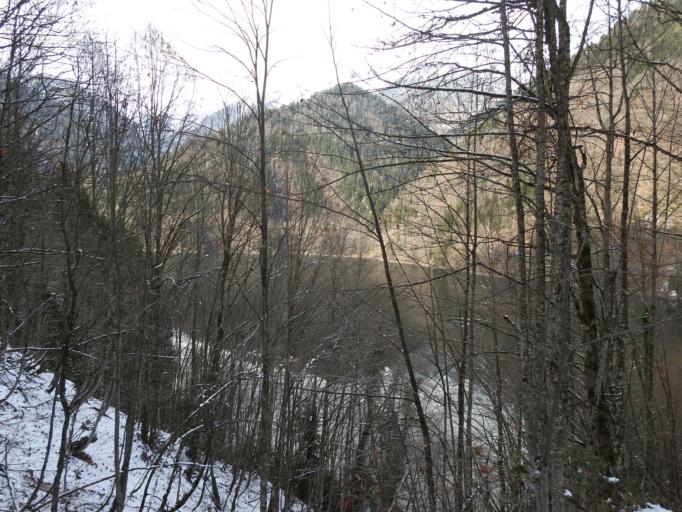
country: GE
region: Abkhazia
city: Gagra
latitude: 43.4786
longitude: 40.5525
